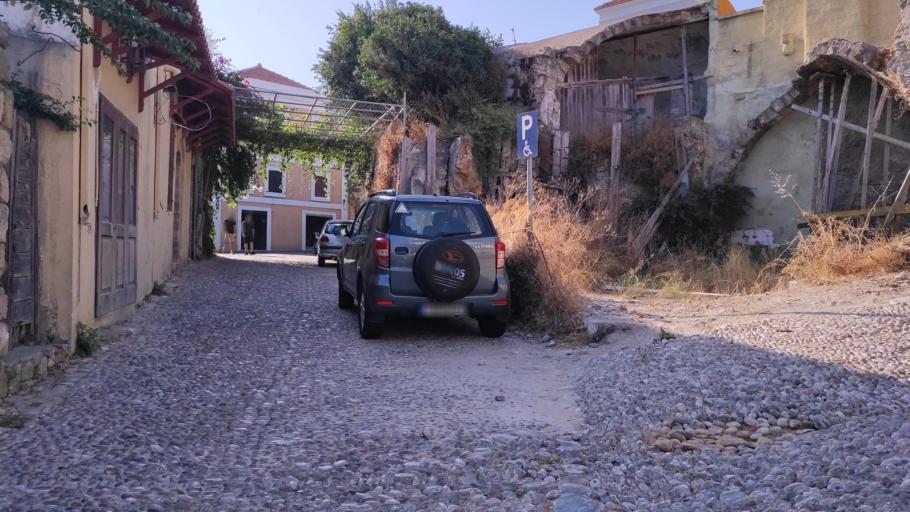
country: GR
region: South Aegean
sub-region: Nomos Dodekanisou
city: Rodos
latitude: 36.4411
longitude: 28.2278
